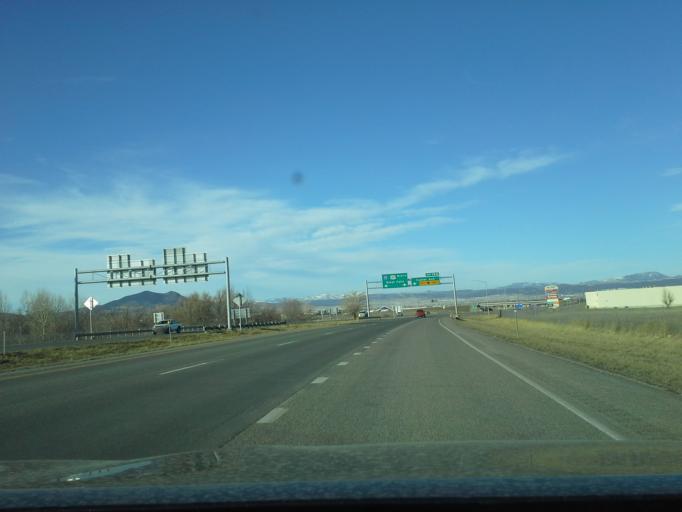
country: US
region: Montana
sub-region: Lewis and Clark County
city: Helena
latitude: 46.6102
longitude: -112.0097
